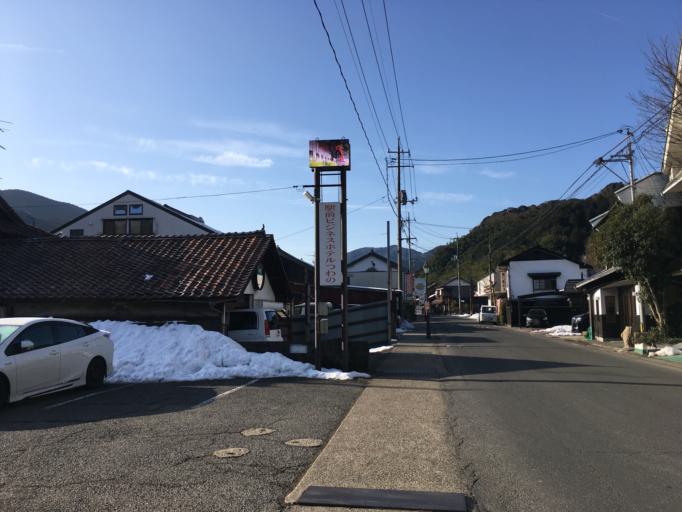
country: JP
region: Shimane
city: Masuda
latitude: 34.4717
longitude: 131.7739
